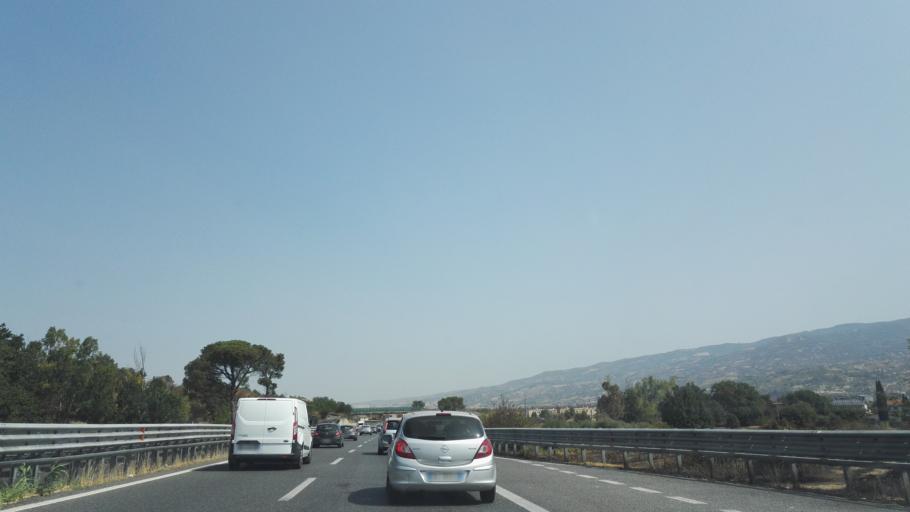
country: IT
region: Calabria
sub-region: Provincia di Cosenza
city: Quattromiglia
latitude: 39.3620
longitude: 16.2343
